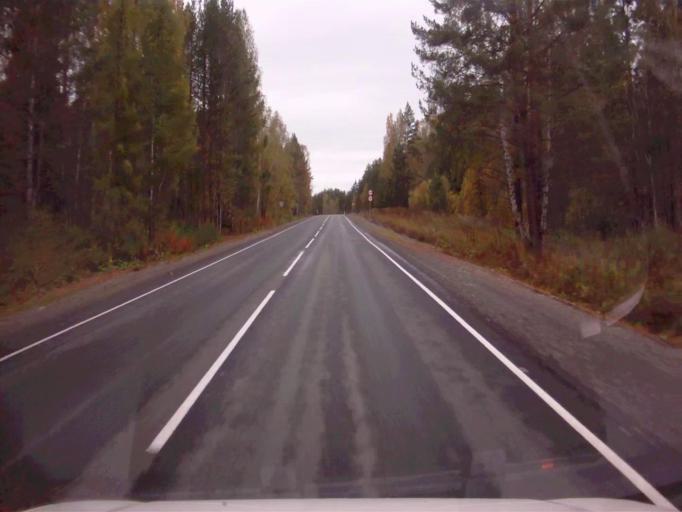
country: RU
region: Chelyabinsk
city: Nyazepetrovsk
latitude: 56.0587
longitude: 59.7328
